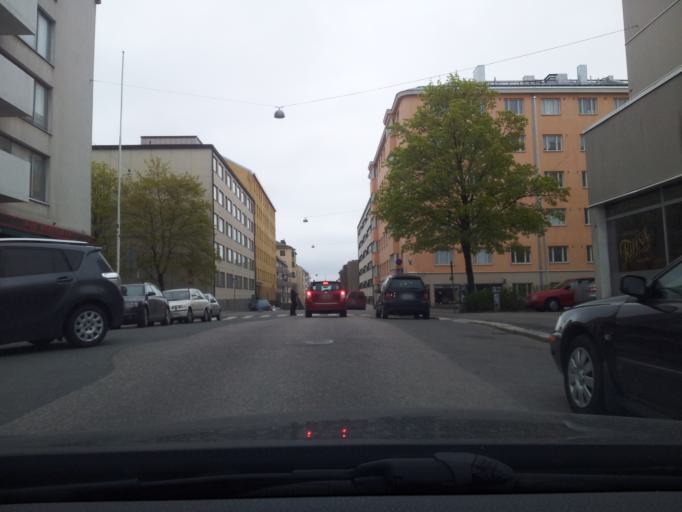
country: FI
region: Uusimaa
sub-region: Helsinki
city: Helsinki
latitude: 60.1850
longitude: 24.9426
